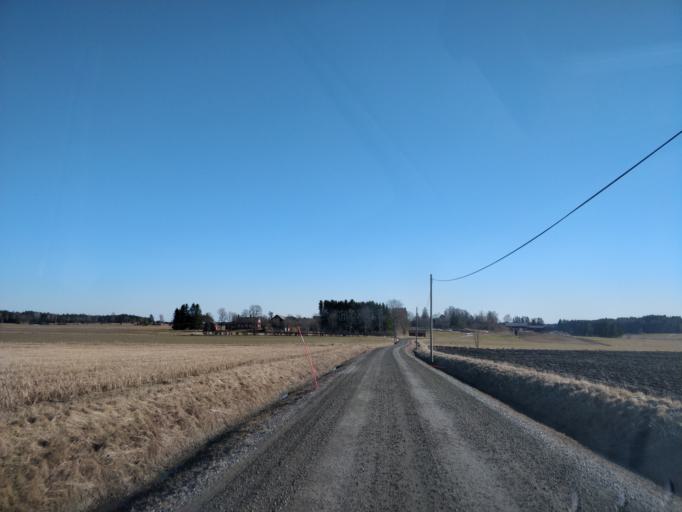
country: SE
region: Uppsala
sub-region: Enkopings Kommun
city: Enkoping
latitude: 59.8180
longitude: 17.1225
